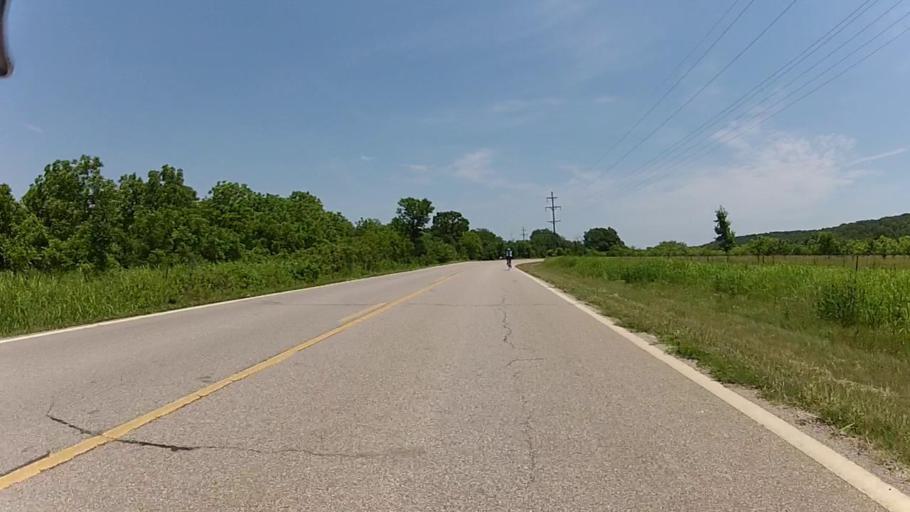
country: US
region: Kansas
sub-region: Chautauqua County
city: Sedan
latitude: 37.1200
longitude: -96.2248
